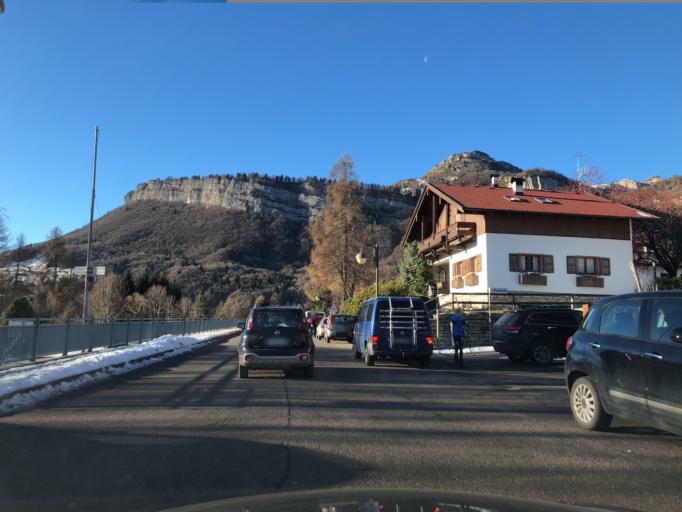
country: IT
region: Trentino-Alto Adige
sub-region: Provincia di Trento
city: Brentonico
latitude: 45.7989
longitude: 10.9201
